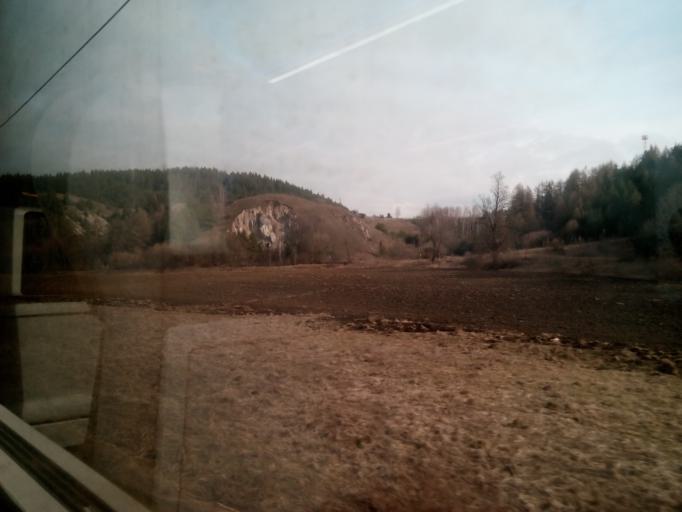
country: SK
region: Zilinsky
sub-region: Okres Zilina
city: Liptovsky Hradok
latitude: 49.0516
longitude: 19.6989
